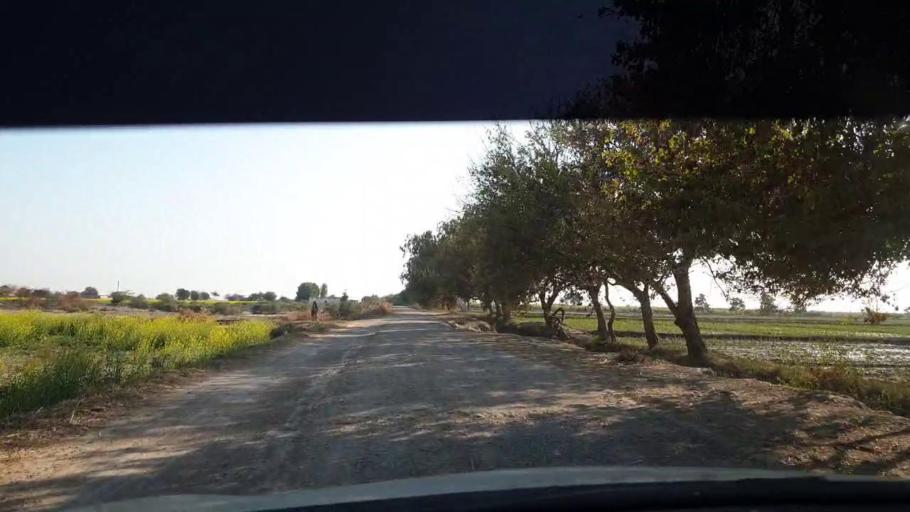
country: PK
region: Sindh
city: Berani
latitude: 25.7996
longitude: 68.9260
